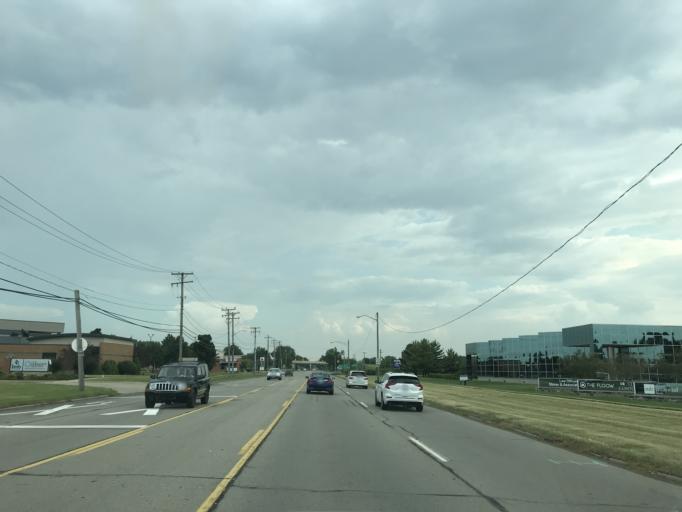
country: US
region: Michigan
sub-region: Wayne County
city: Southgate
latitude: 42.2122
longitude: -83.2292
